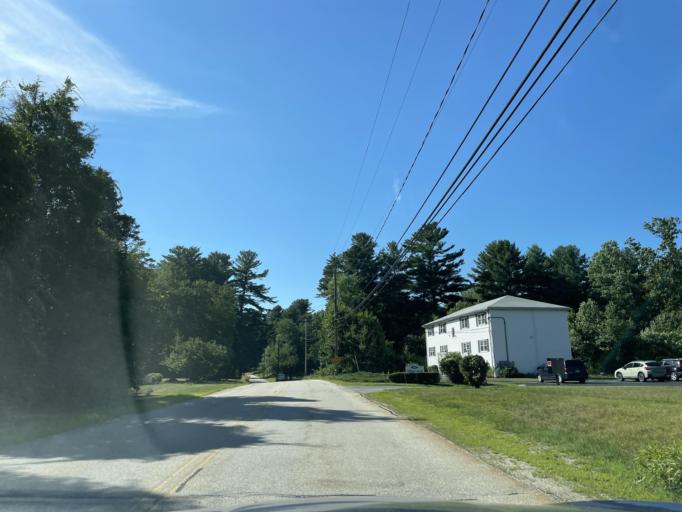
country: US
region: Massachusetts
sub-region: Worcester County
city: Oxford
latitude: 42.1174
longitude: -71.8895
